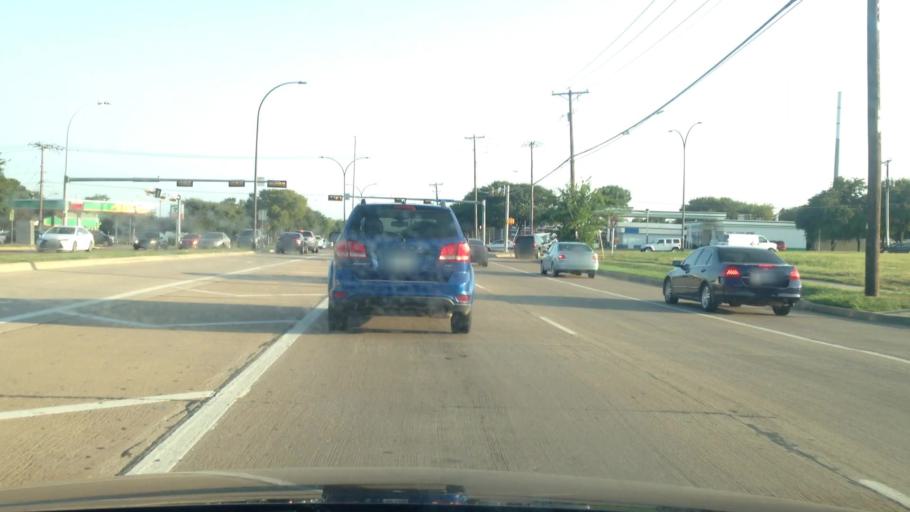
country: US
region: Texas
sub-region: Tarrant County
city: Dalworthington Gardens
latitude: 32.6712
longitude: -97.1150
